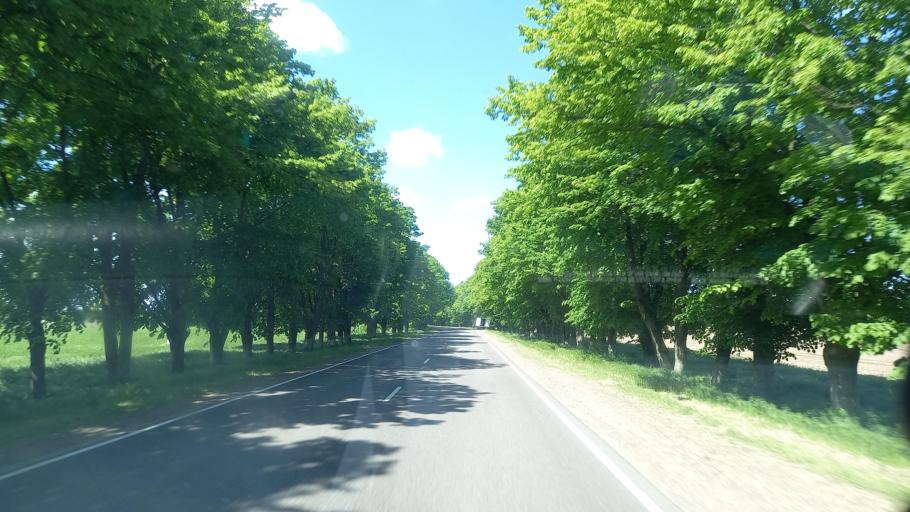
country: RU
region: Krasnodarskiy
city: Novoukrainskoye
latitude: 45.3778
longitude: 40.4797
